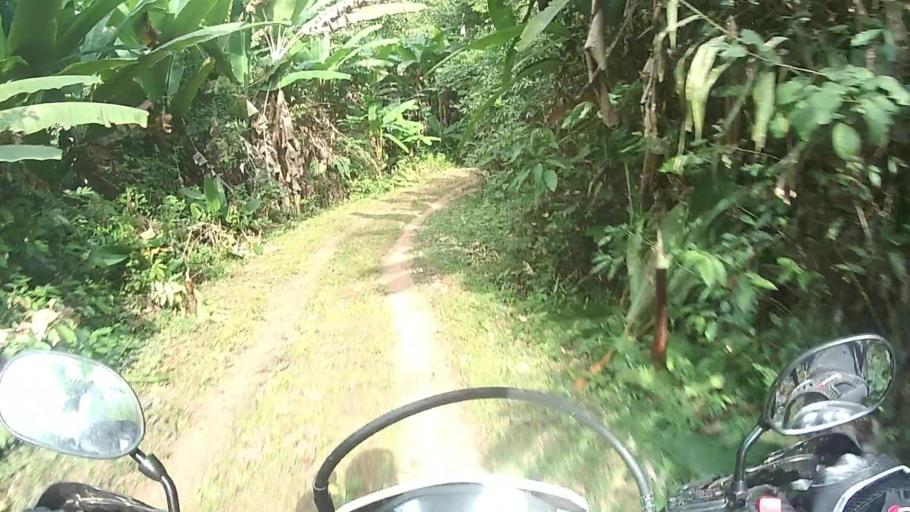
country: TH
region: Lampang
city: Mueang Pan
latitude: 18.8072
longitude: 99.3895
